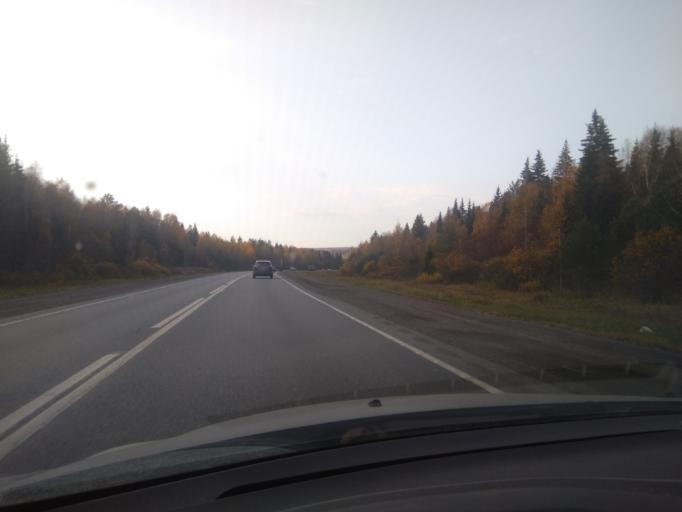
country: RU
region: Sverdlovsk
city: Druzhinino
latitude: 56.8136
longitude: 59.5585
